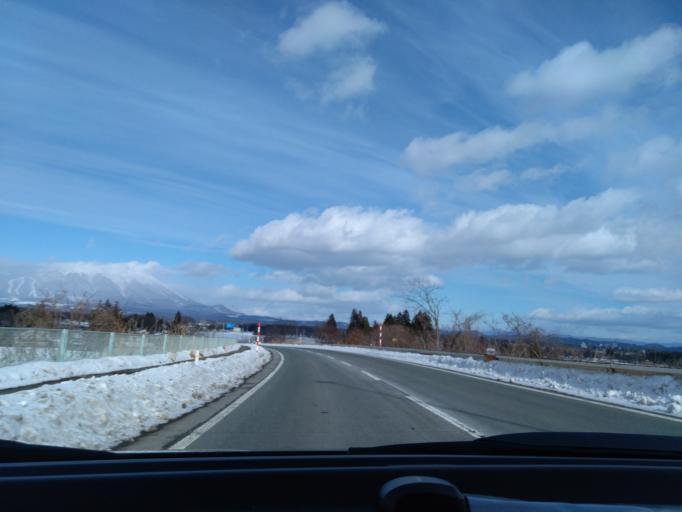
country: JP
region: Iwate
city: Shizukuishi
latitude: 39.6936
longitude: 140.9351
